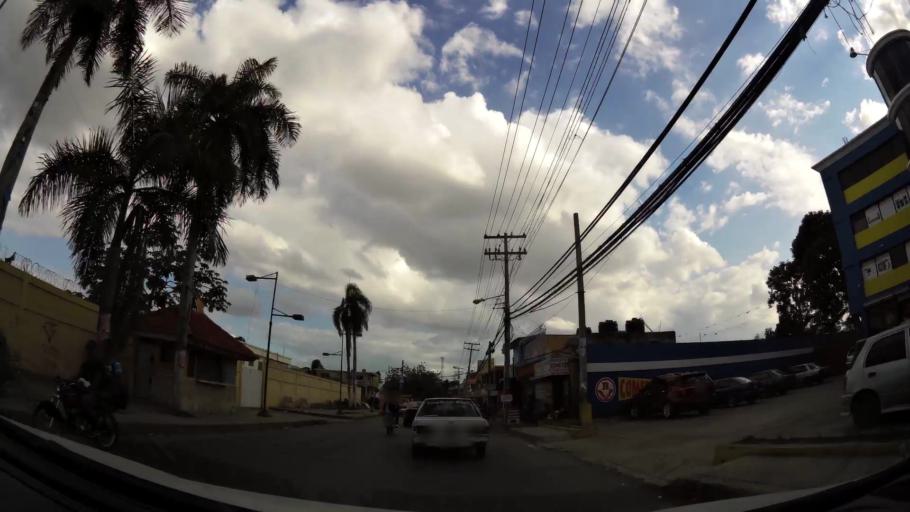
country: DO
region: Nacional
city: Ensanche Luperon
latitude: 18.5549
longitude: -69.9040
